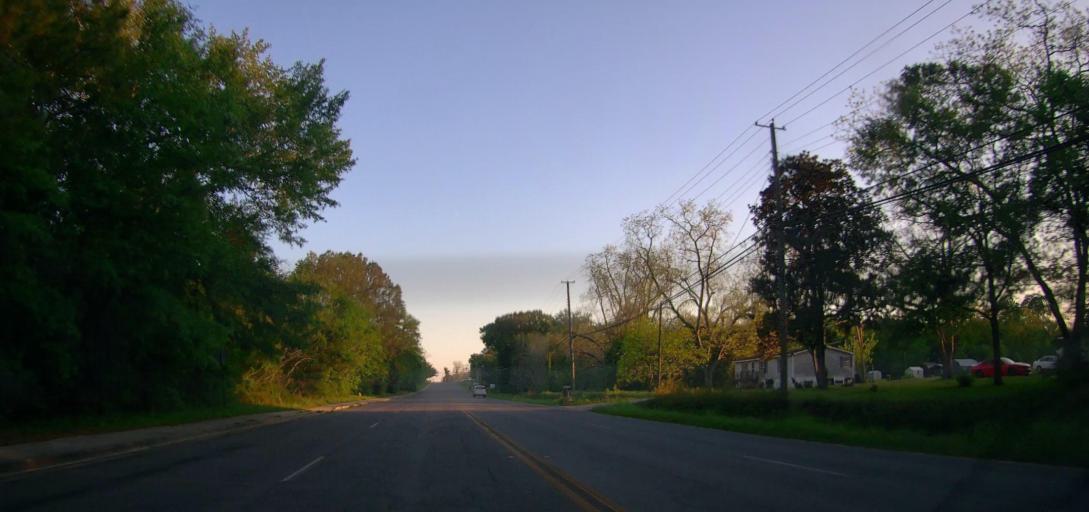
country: US
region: Georgia
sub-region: Ben Hill County
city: Fitzgerald
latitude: 31.7039
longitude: -83.2611
